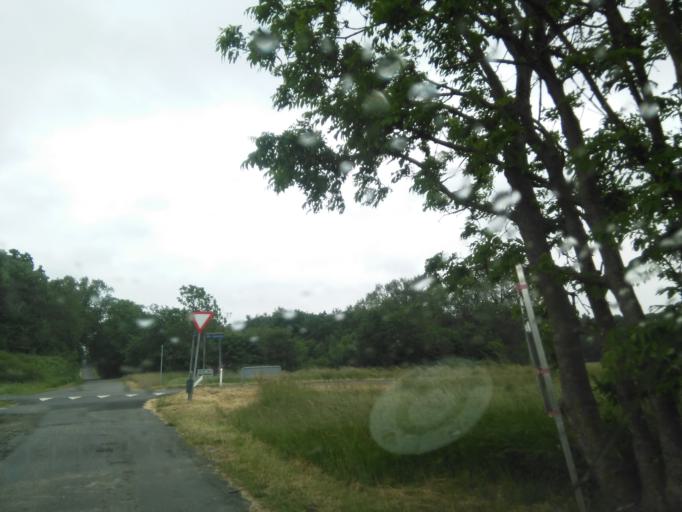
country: DK
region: Capital Region
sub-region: Bornholm Kommune
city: Akirkeby
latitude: 55.0467
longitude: 14.8337
